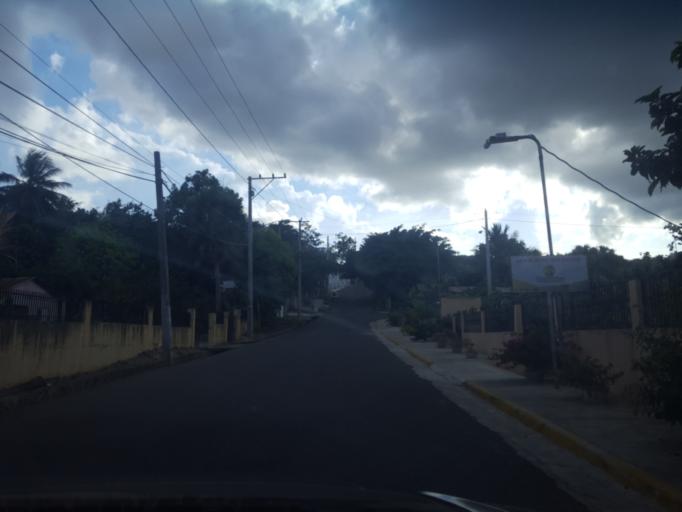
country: DO
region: Santiago
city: Licey al Medio
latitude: 19.3737
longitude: -70.6400
